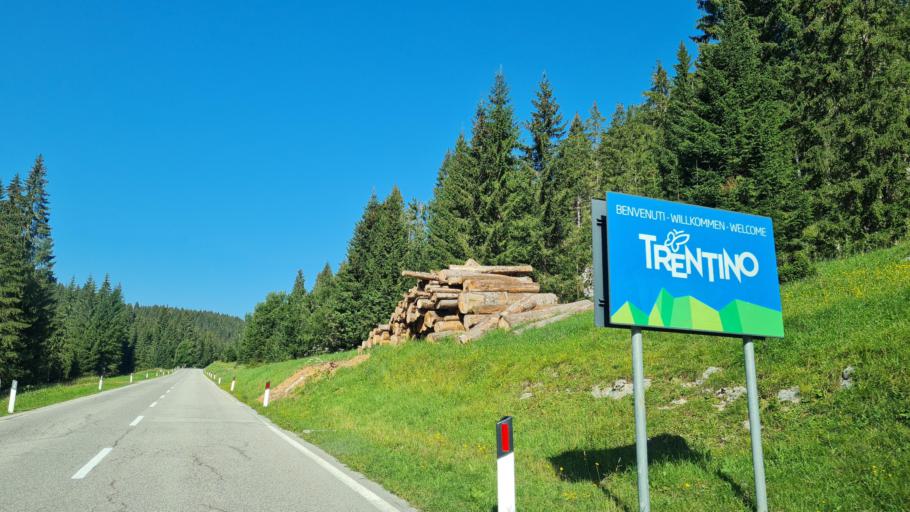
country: IT
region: Trentino-Alto Adige
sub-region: Provincia di Trento
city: Luserna
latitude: 45.9502
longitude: 11.3743
